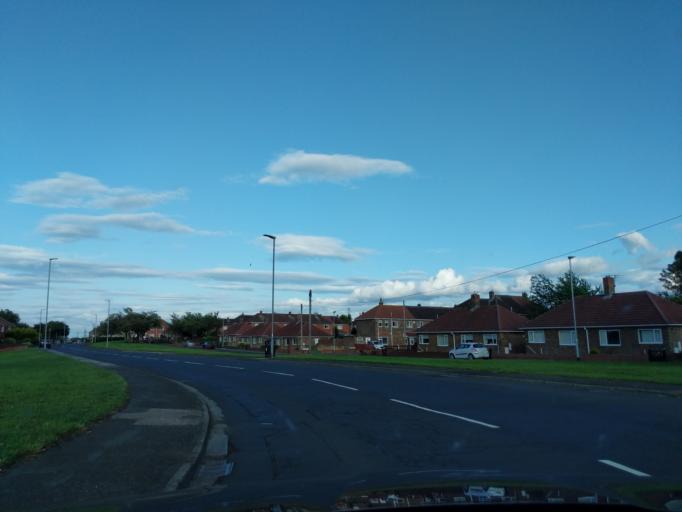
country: GB
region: England
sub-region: Northumberland
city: Bedlington
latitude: 55.1328
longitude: -1.5783
